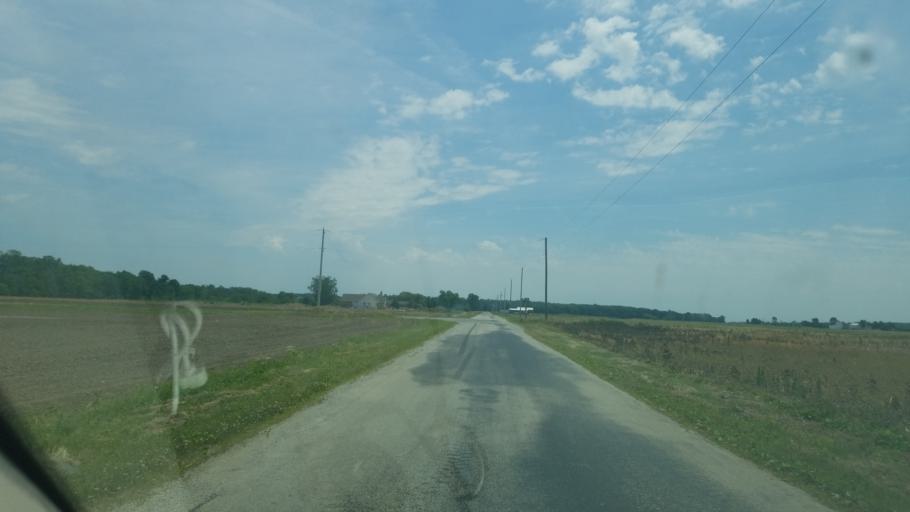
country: US
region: Ohio
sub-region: Wood County
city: North Baltimore
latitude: 41.2219
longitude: -83.6030
